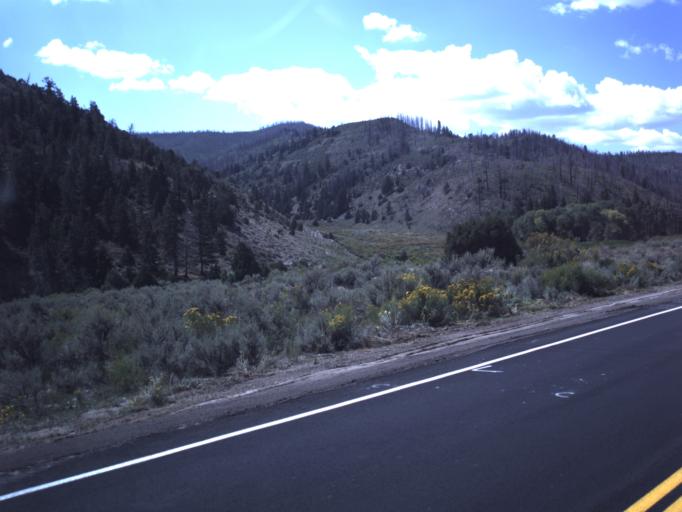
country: US
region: Utah
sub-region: Carbon County
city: Helper
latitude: 39.9314
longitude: -110.6747
